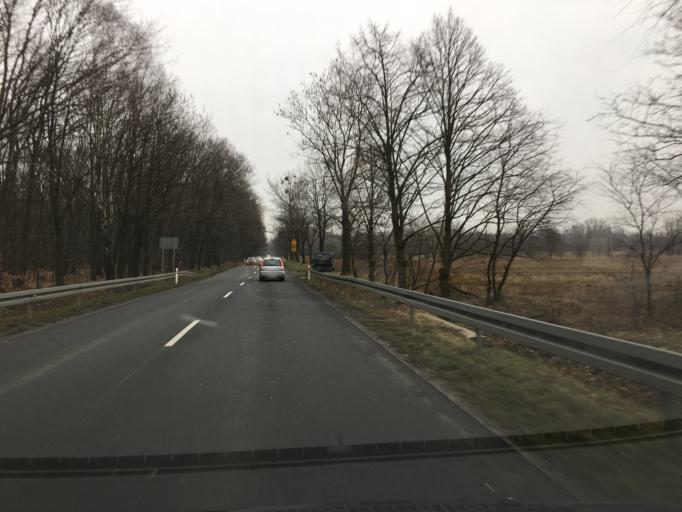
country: PL
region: Opole Voivodeship
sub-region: Powiat kedzierzynsko-kozielski
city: Bierawa
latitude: 50.3043
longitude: 18.2299
